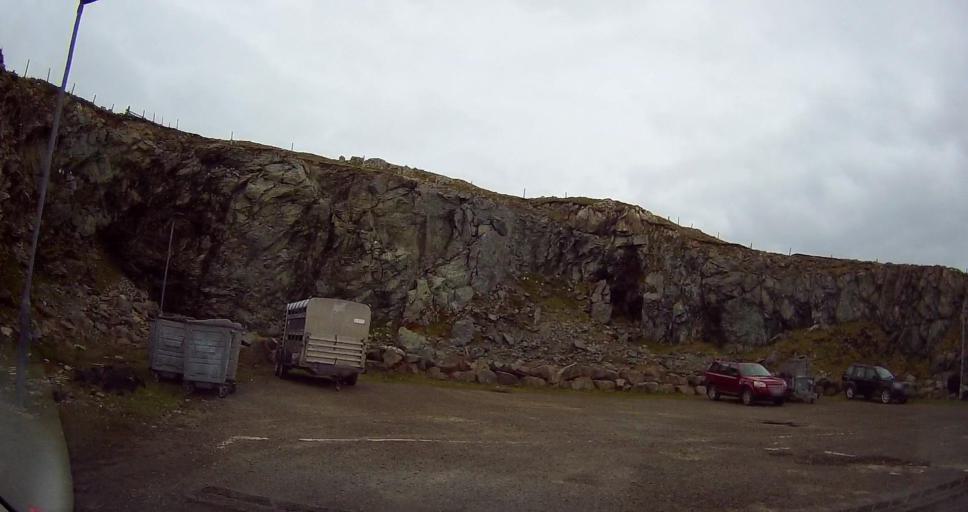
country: GB
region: Scotland
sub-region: Shetland Islands
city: Shetland
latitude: 60.6833
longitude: -0.9649
